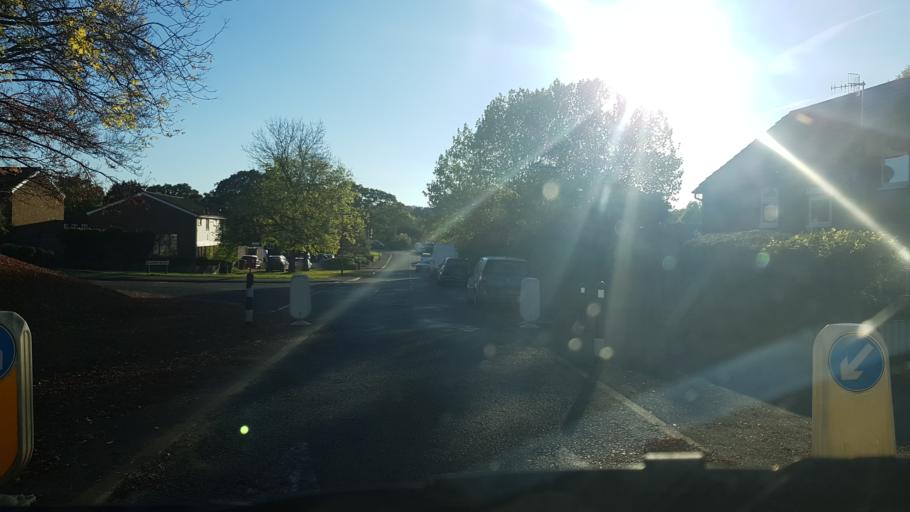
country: GB
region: England
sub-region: Surrey
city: Guildford
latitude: 51.2506
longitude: -0.6093
